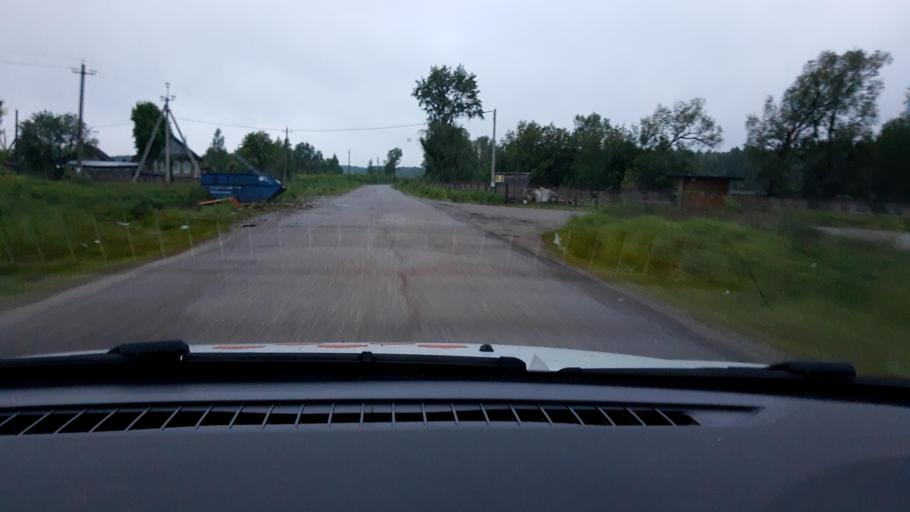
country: RU
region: Nizjnij Novgorod
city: Novaya Balakhna
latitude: 56.6326
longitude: 43.6167
